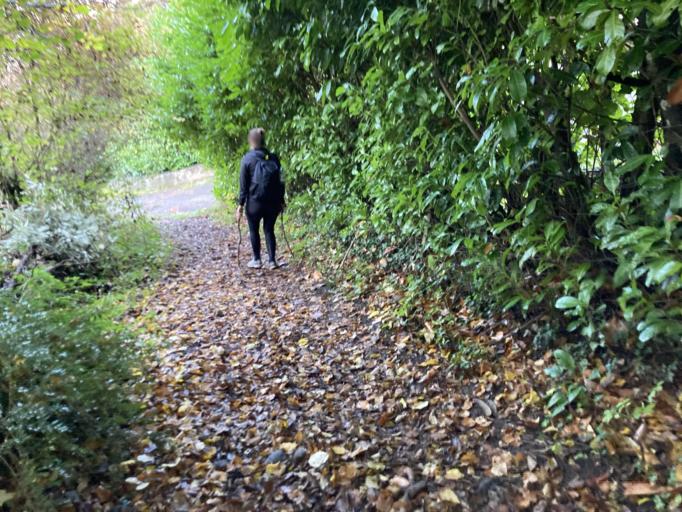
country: FR
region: Rhone-Alpes
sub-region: Departement de la Haute-Savoie
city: Sevrier
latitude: 45.8614
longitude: 6.1368
